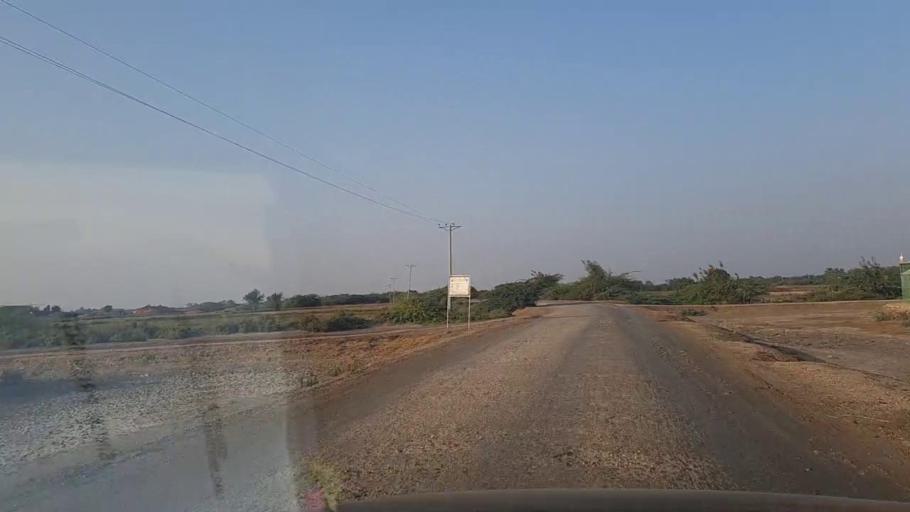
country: PK
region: Sindh
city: Keti Bandar
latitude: 24.2829
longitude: 67.5876
